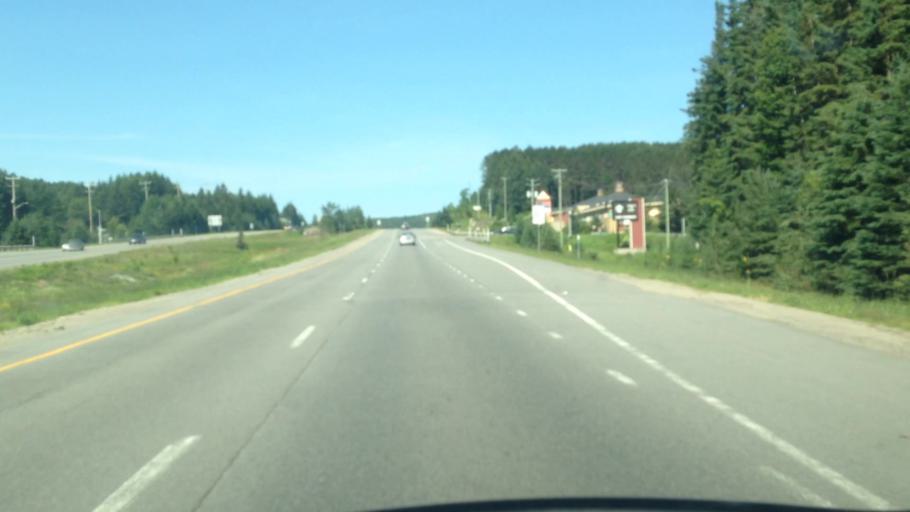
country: CA
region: Quebec
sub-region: Laurentides
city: Mont-Tremblant
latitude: 46.1156
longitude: -74.5794
